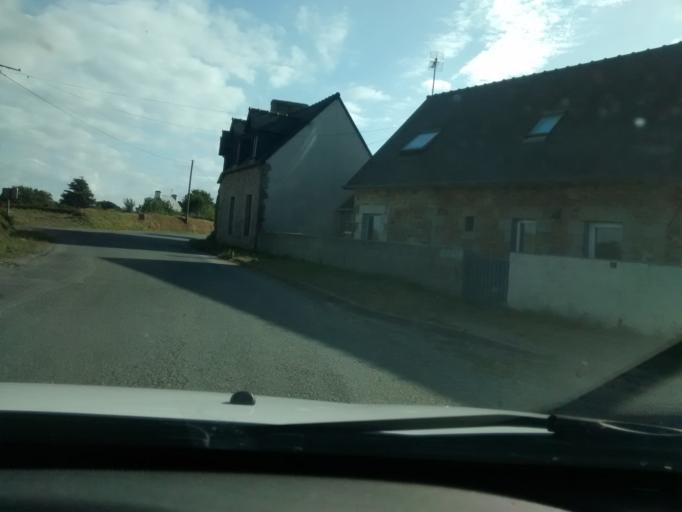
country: FR
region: Brittany
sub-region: Departement des Cotes-d'Armor
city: Penvenan
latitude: 48.8031
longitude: -3.2974
